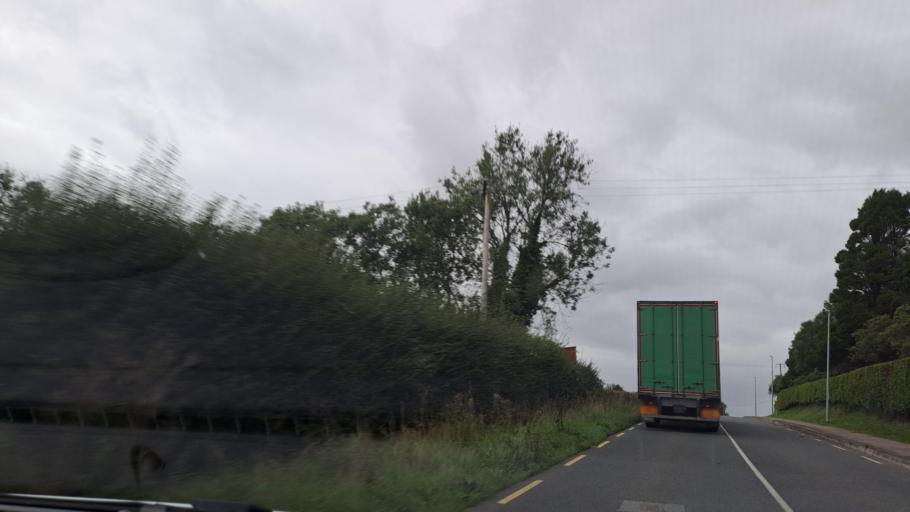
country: IE
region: Ulster
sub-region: County Monaghan
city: Monaghan
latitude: 54.1354
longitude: -6.9091
